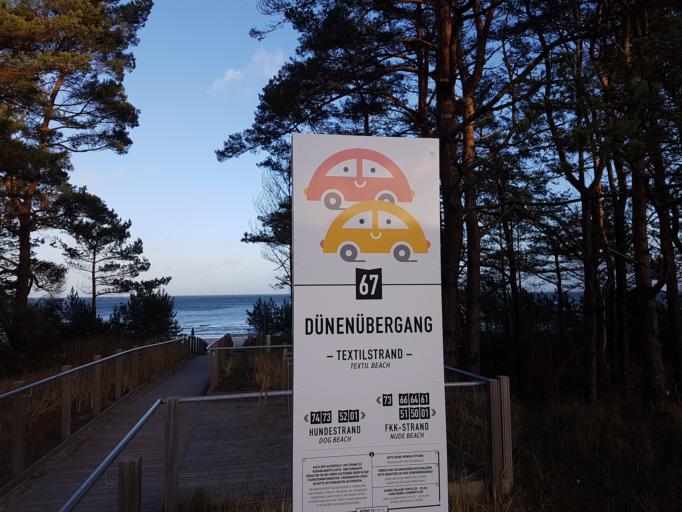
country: DE
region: Mecklenburg-Vorpommern
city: Ostseebad Binz
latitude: 54.4280
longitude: 13.5846
